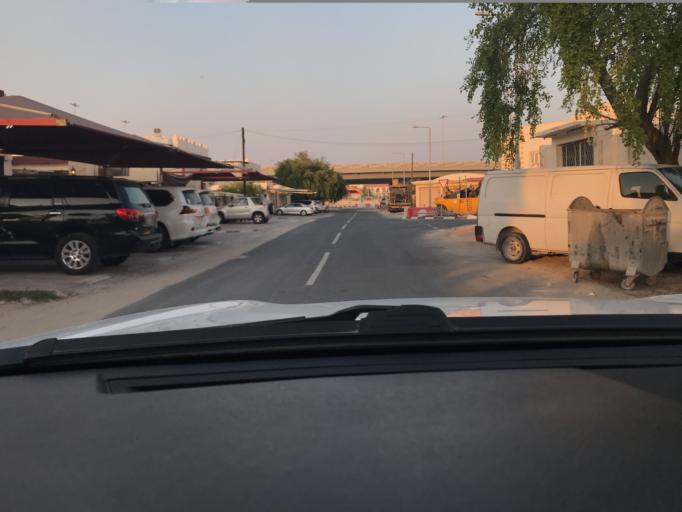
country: QA
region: Baladiyat ad Dawhah
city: Doha
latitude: 25.2531
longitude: 51.5058
